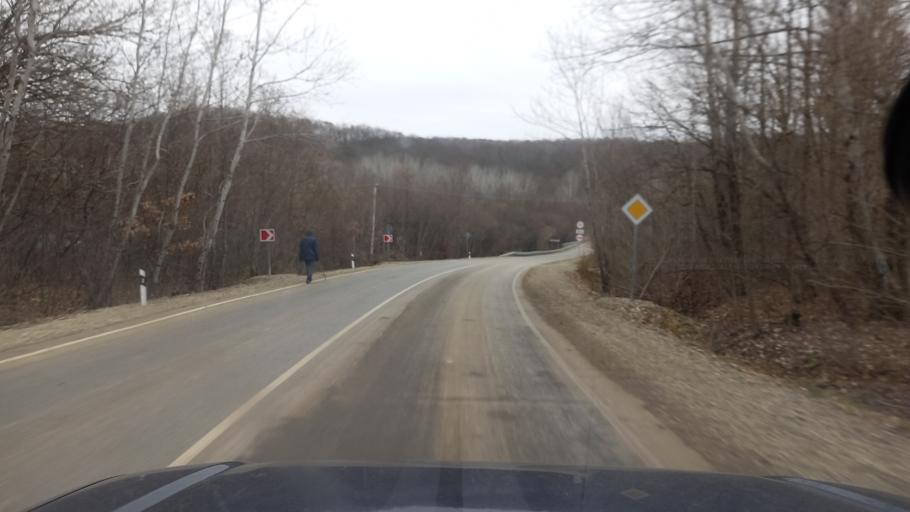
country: RU
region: Krasnodarskiy
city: Saratovskaya
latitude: 44.5436
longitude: 39.2931
